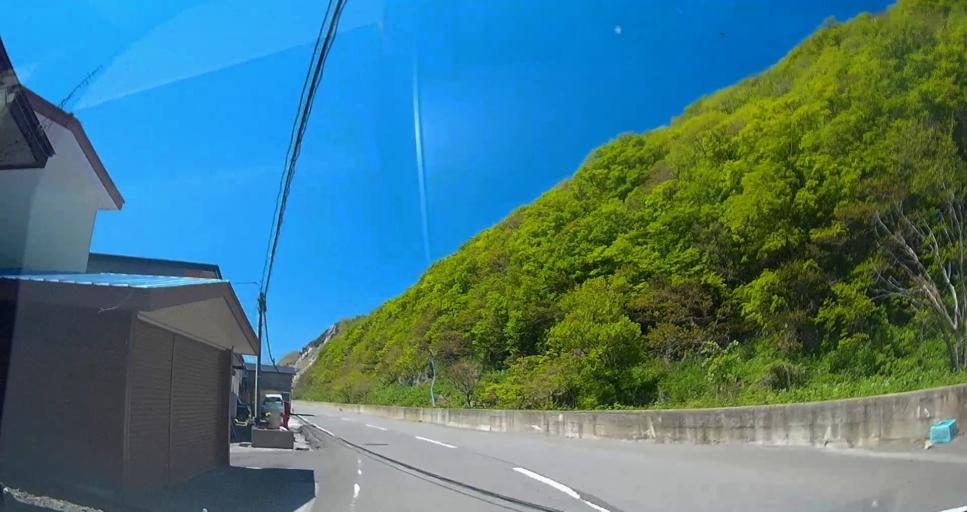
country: JP
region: Aomori
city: Mutsu
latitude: 41.3279
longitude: 140.8111
